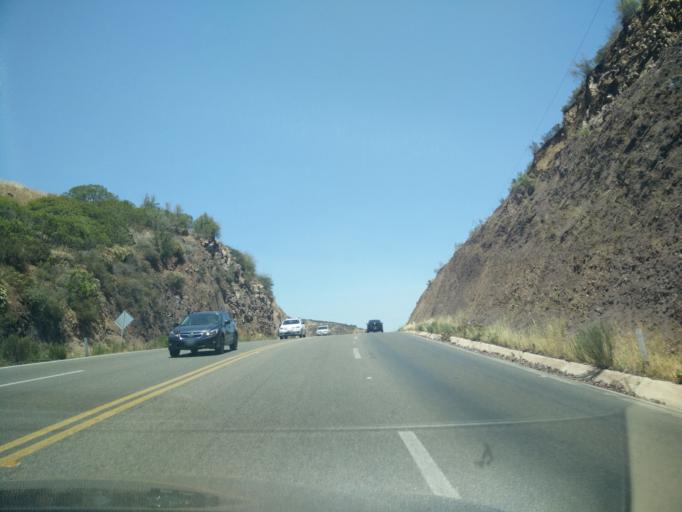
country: MX
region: Baja California
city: El Sauzal
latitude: 31.9389
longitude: -116.6703
